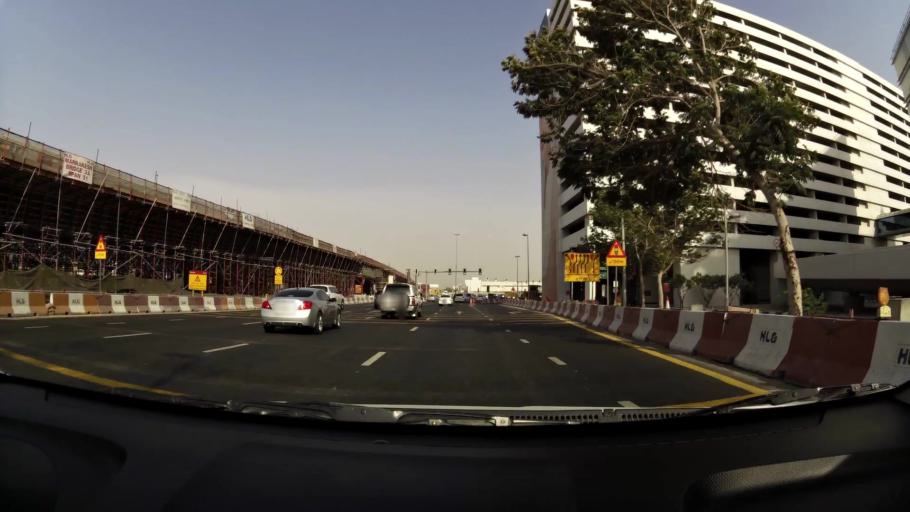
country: AE
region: Ash Shariqah
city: Sharjah
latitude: 25.2416
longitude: 55.3674
